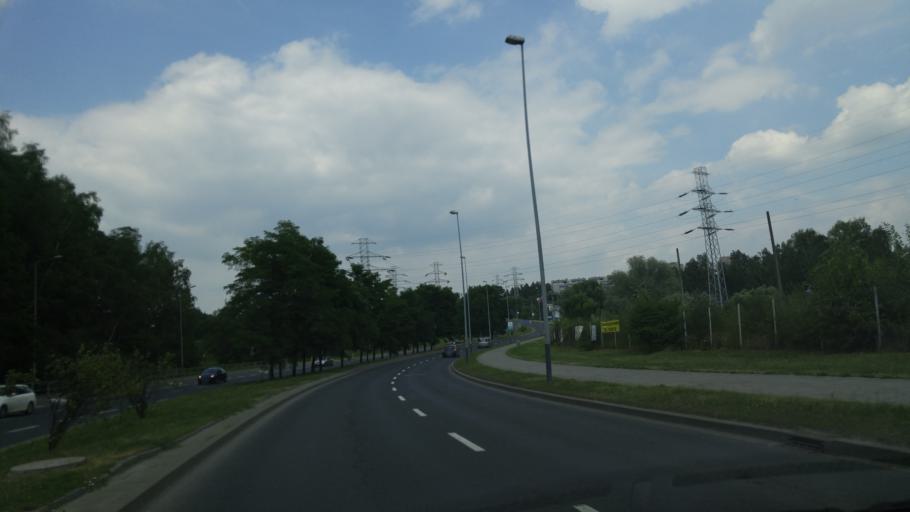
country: PL
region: Lesser Poland Voivodeship
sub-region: Krakow
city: Krakow
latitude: 50.0106
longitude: 19.9441
